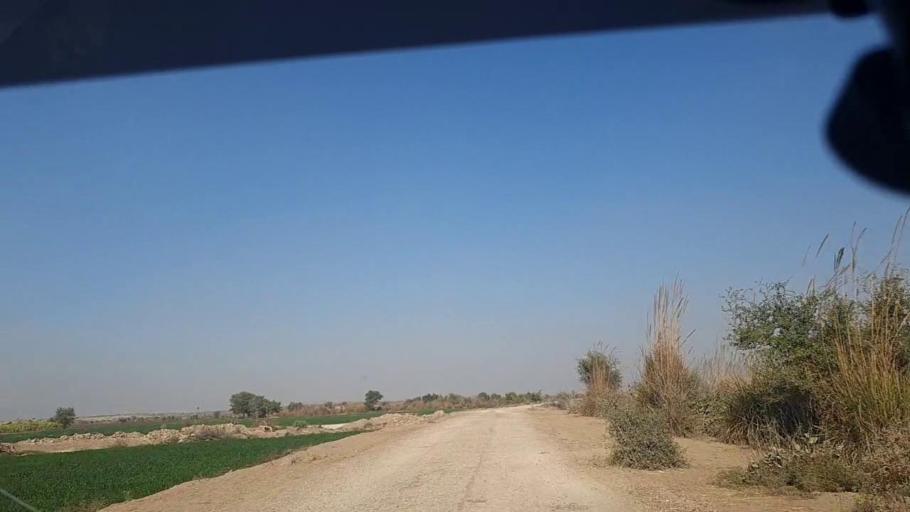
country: PK
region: Sindh
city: Khanpur
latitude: 27.5608
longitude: 69.3358
